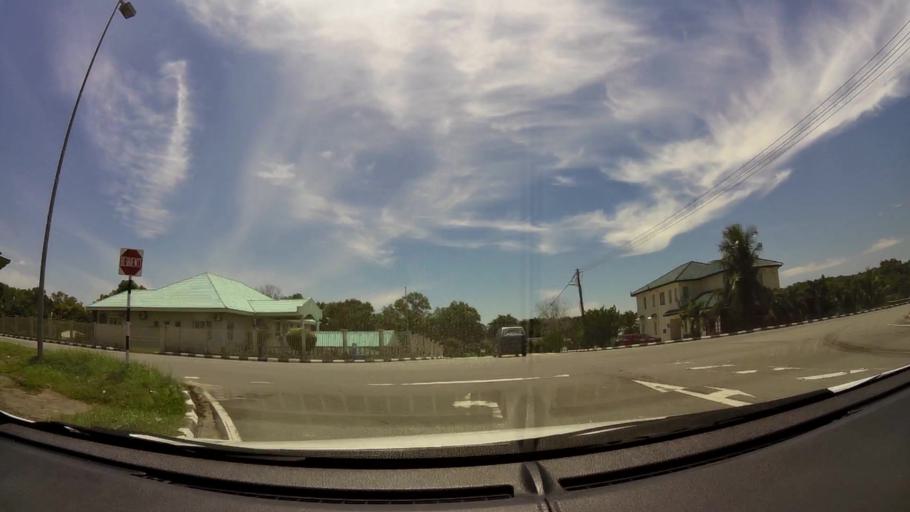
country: BN
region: Brunei and Muara
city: Bandar Seri Begawan
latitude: 4.9383
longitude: 114.9553
